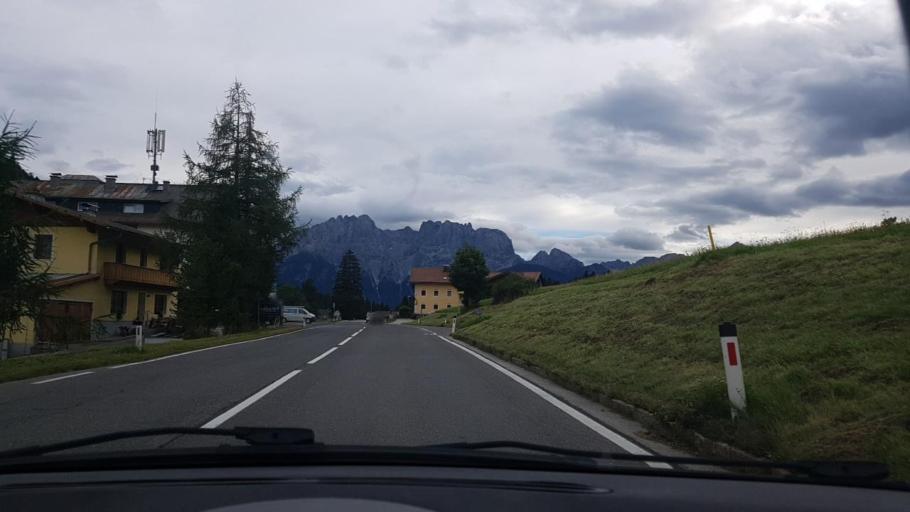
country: AT
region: Carinthia
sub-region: Politischer Bezirk Spittal an der Drau
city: Winklern
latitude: 46.8560
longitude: 12.8588
